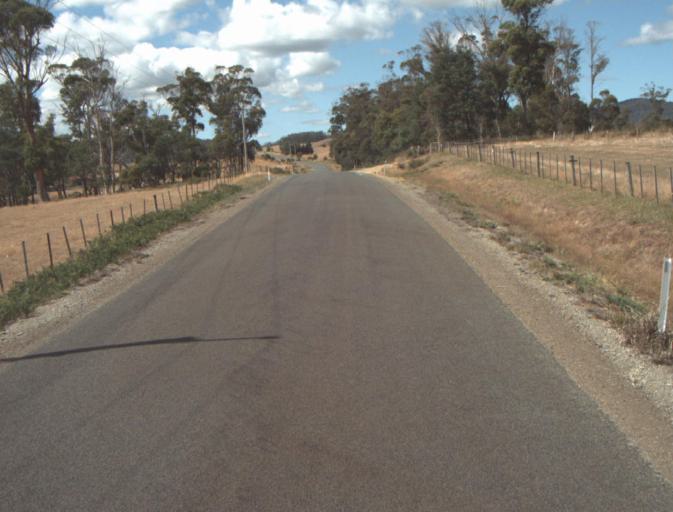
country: AU
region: Tasmania
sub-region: Launceston
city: Mayfield
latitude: -41.2281
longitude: 147.1439
